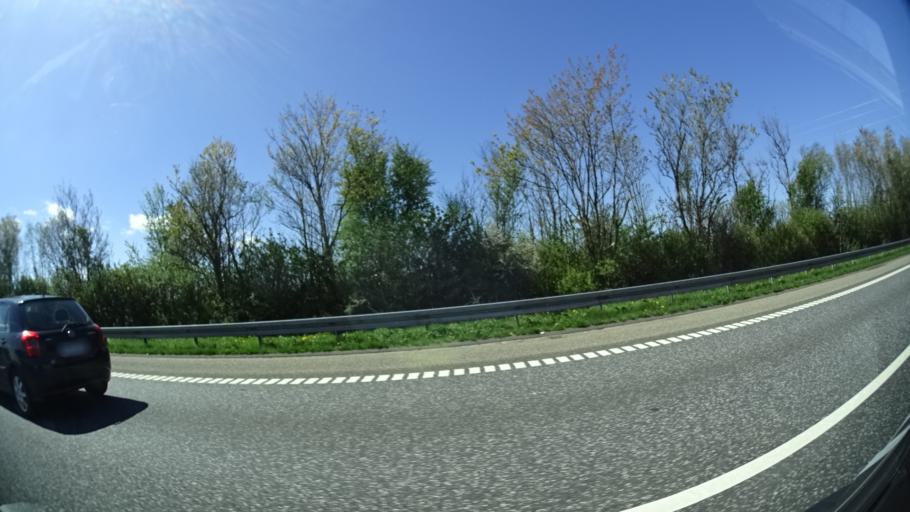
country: DK
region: Central Jutland
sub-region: Arhus Kommune
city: Trige
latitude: 56.2752
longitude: 10.1331
